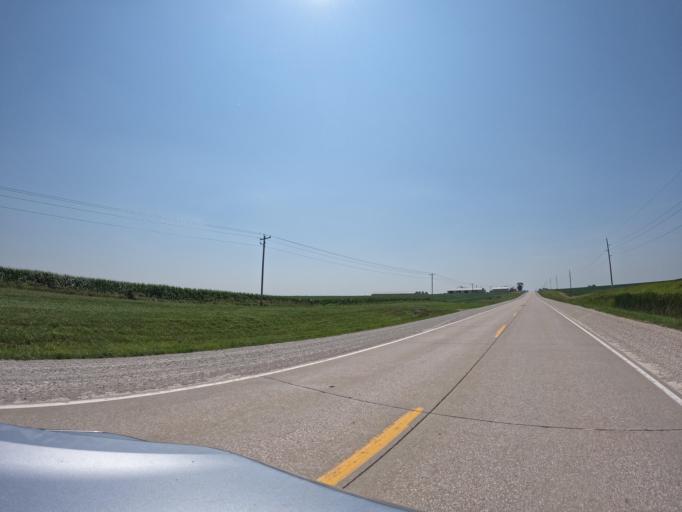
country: US
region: Iowa
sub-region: Keokuk County
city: Sigourney
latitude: 41.3368
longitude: -92.2445
